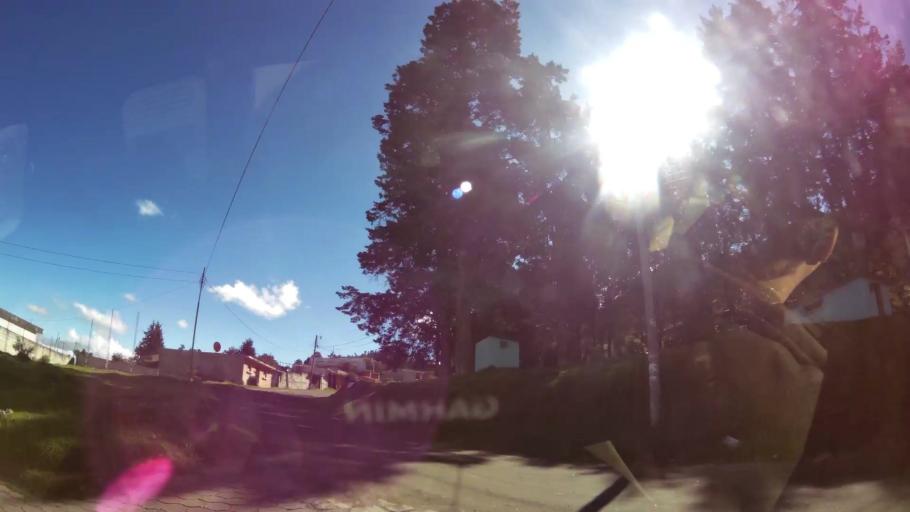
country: GT
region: Quetzaltenango
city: Quetzaltenango
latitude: 14.8349
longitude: -91.5020
